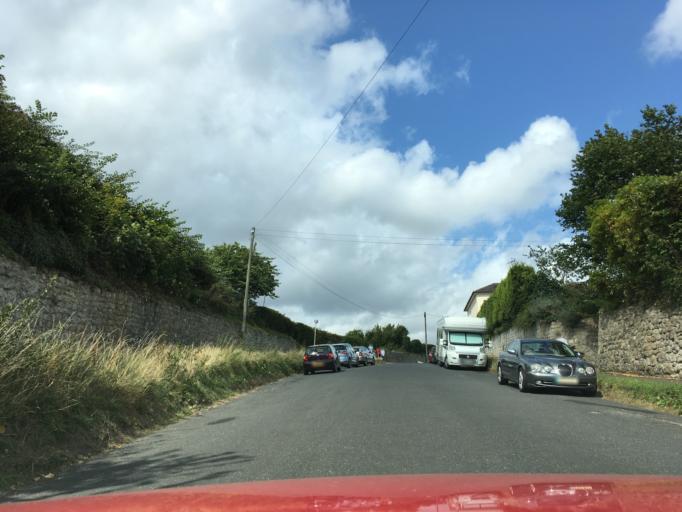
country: GB
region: England
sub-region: Kent
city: Maidstone
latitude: 51.2421
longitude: 0.5183
